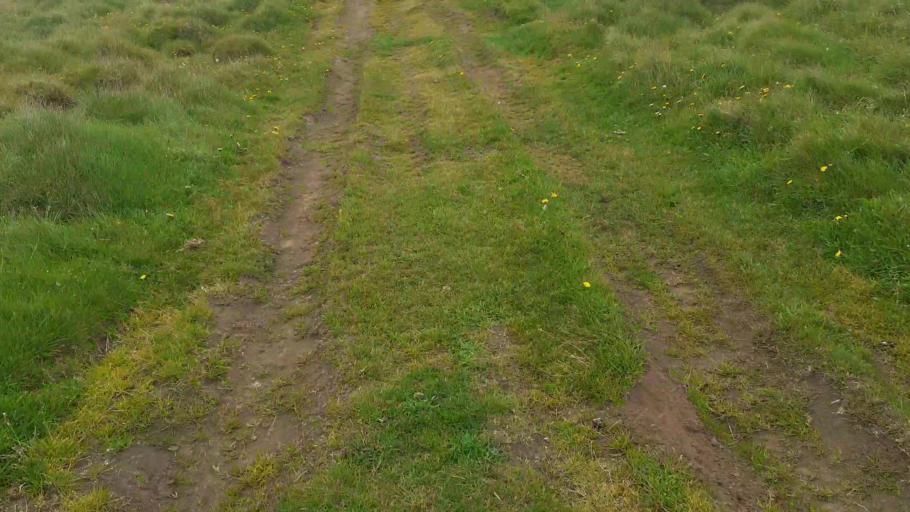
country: IS
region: Northeast
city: Dalvik
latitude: 66.5419
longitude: -17.9845
